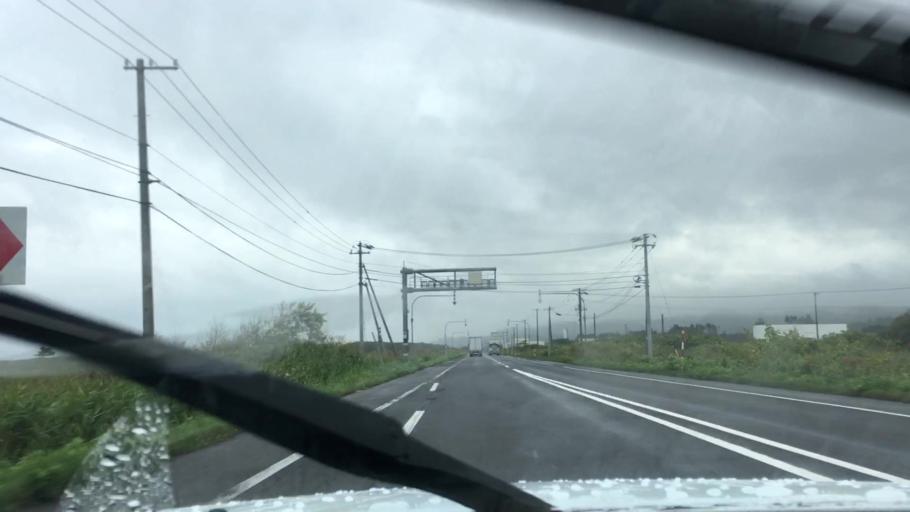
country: JP
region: Hokkaido
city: Niseko Town
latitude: 42.3968
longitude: 140.3013
